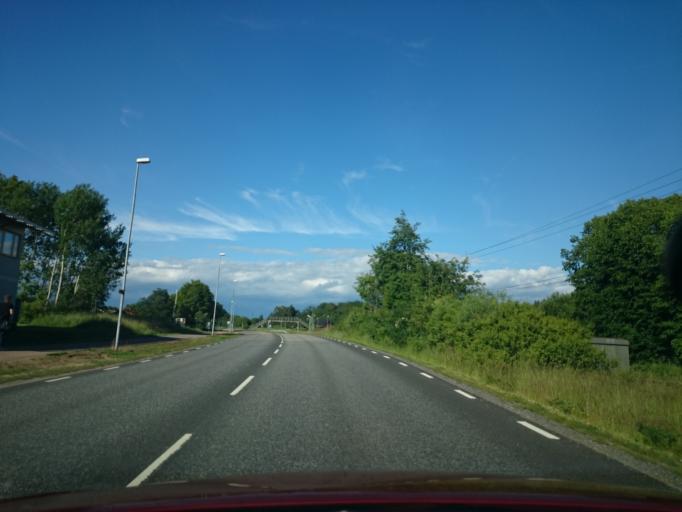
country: SE
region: Vaestra Goetaland
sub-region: Lerums Kommun
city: Stenkullen
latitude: 57.7863
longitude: 12.3063
